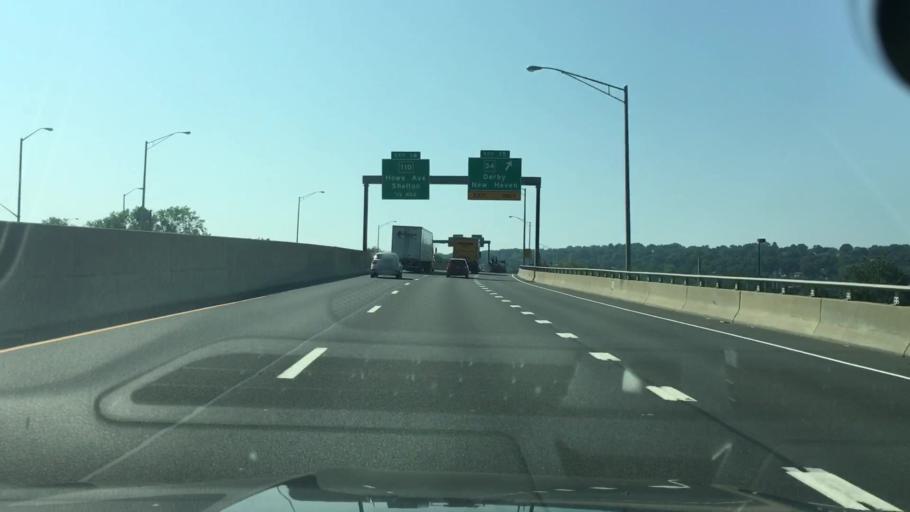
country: US
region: Connecticut
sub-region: New Haven County
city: Derby
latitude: 41.3208
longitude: -73.0845
